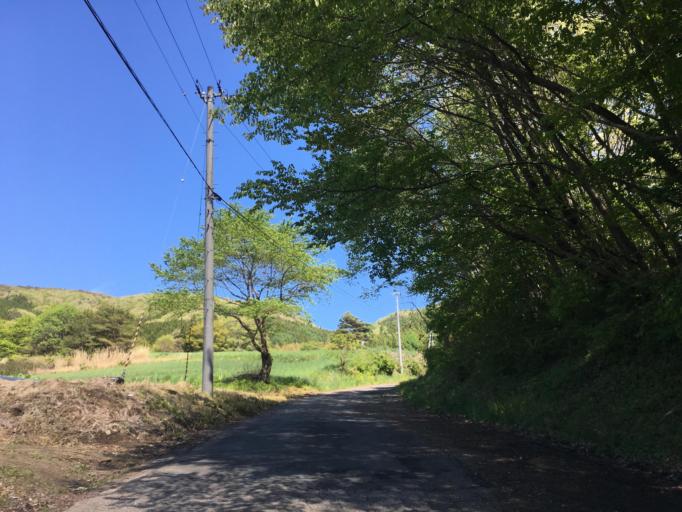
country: JP
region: Fukushima
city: Funehikimachi-funehiki
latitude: 37.3035
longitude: 140.6785
